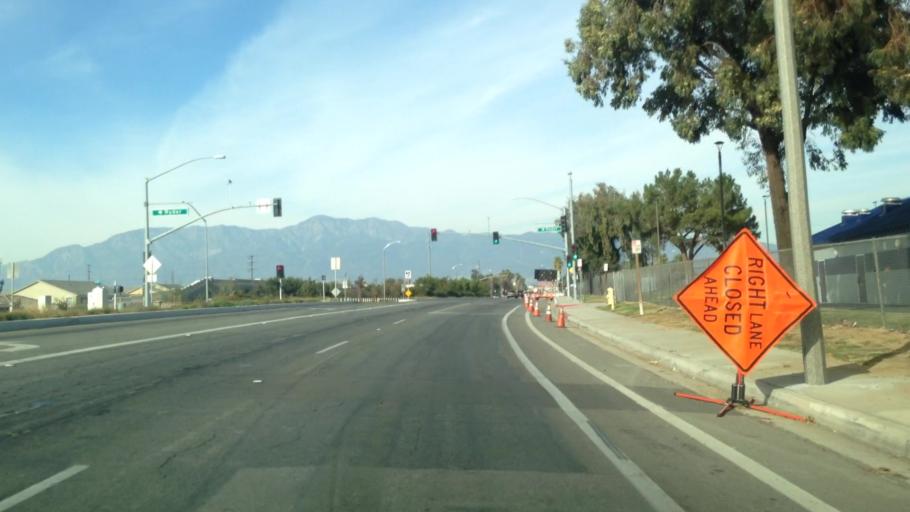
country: US
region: California
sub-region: Riverside County
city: Mira Loma
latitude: 34.0010
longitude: -117.5244
